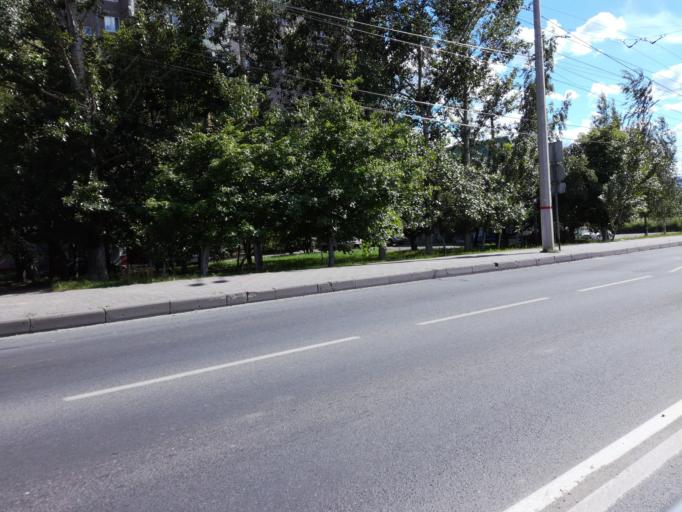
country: RU
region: Kursk
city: Kursk
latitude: 51.7632
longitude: 36.1720
